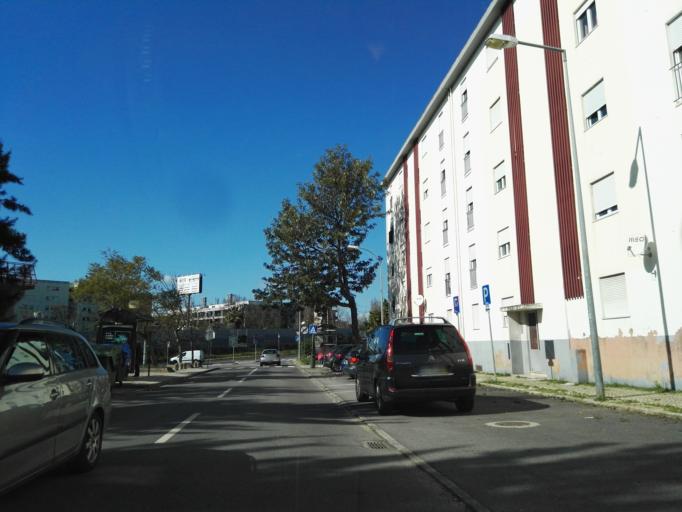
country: PT
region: Lisbon
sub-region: Amadora
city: Amadora
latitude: 38.7360
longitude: -9.2053
